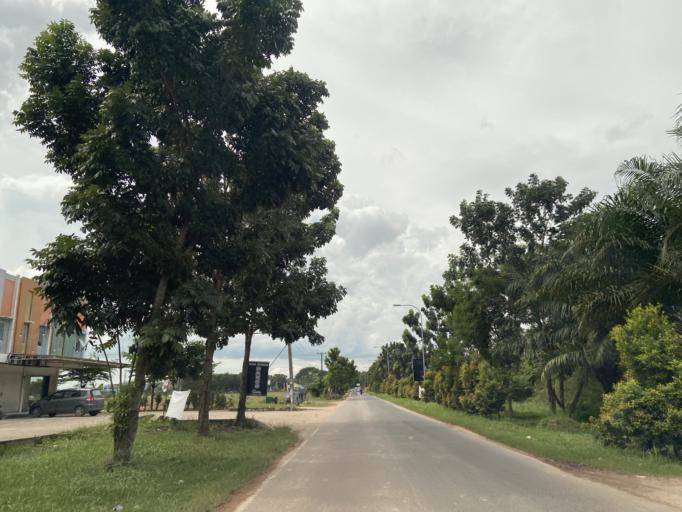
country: SG
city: Singapore
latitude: 1.0415
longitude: 103.9692
